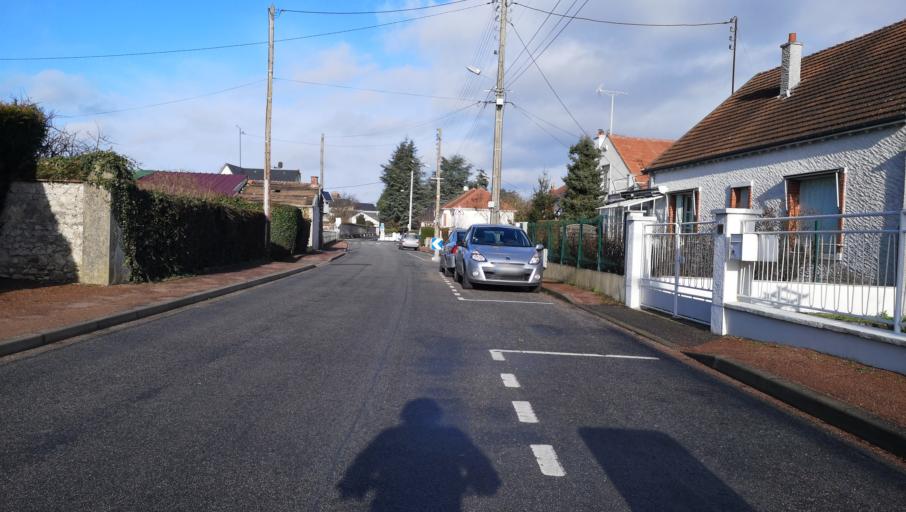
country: FR
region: Centre
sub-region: Departement du Loiret
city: Saint-Pryve-Saint-Mesmin
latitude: 47.8889
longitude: 1.8765
